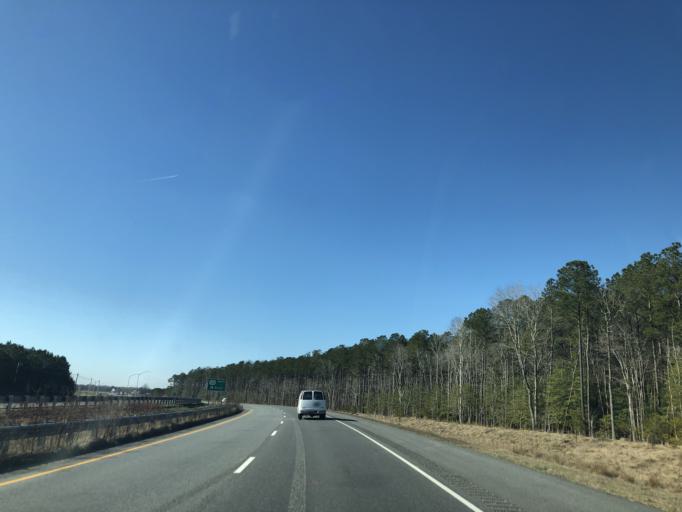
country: US
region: Maryland
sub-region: Worcester County
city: Snow Hill
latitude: 38.2330
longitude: -75.3319
